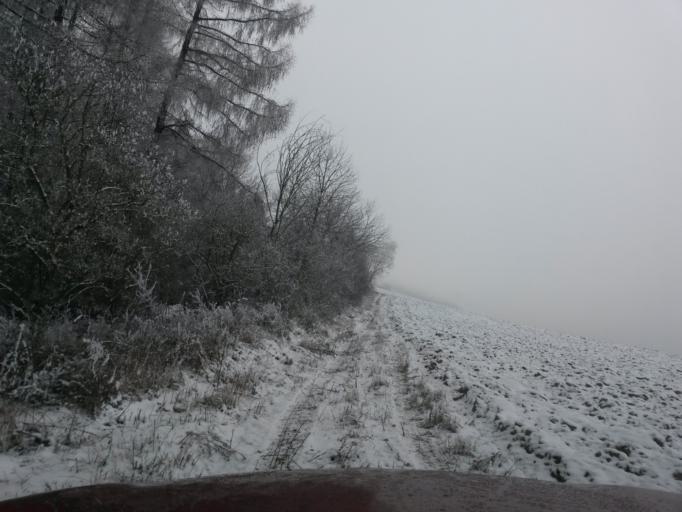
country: SK
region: Presovsky
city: Sabinov
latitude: 48.9798
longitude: 21.0867
